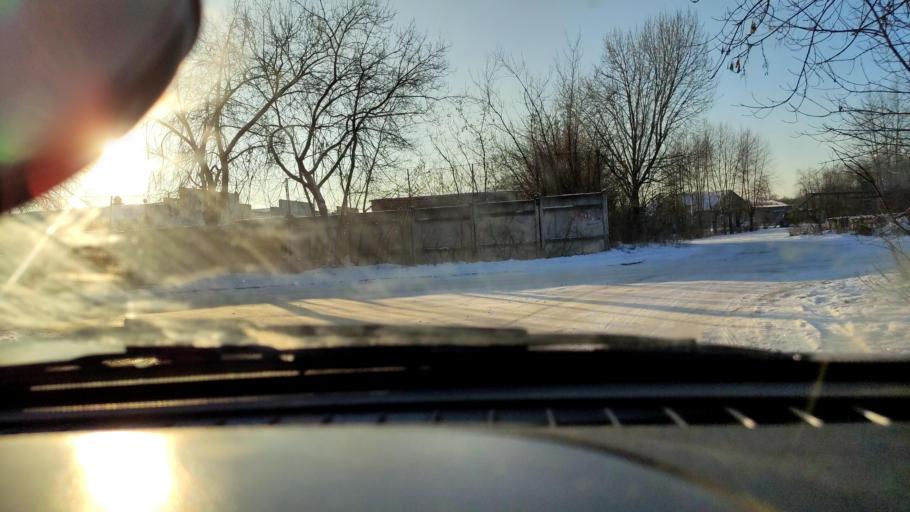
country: RU
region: Perm
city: Kultayevo
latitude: 57.9986
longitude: 55.9321
